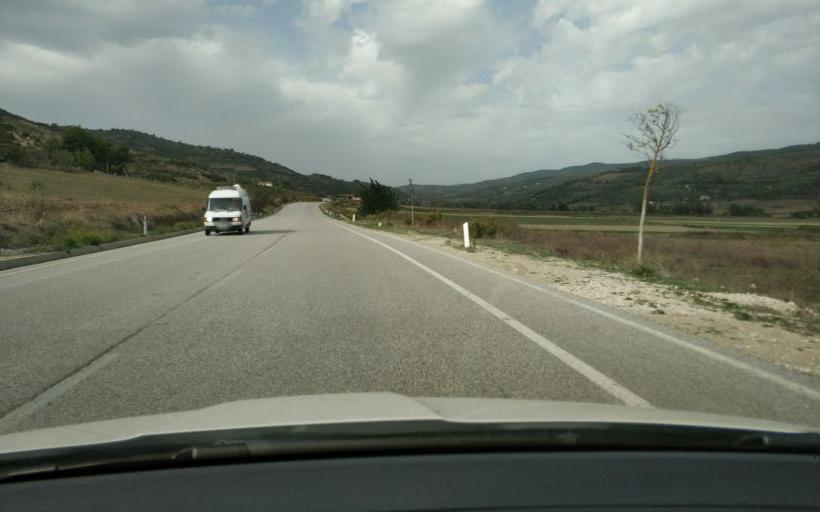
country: AL
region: Gjirokaster
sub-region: Rrethi i Tepelenes
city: Krahes
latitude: 40.4438
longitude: 19.8487
